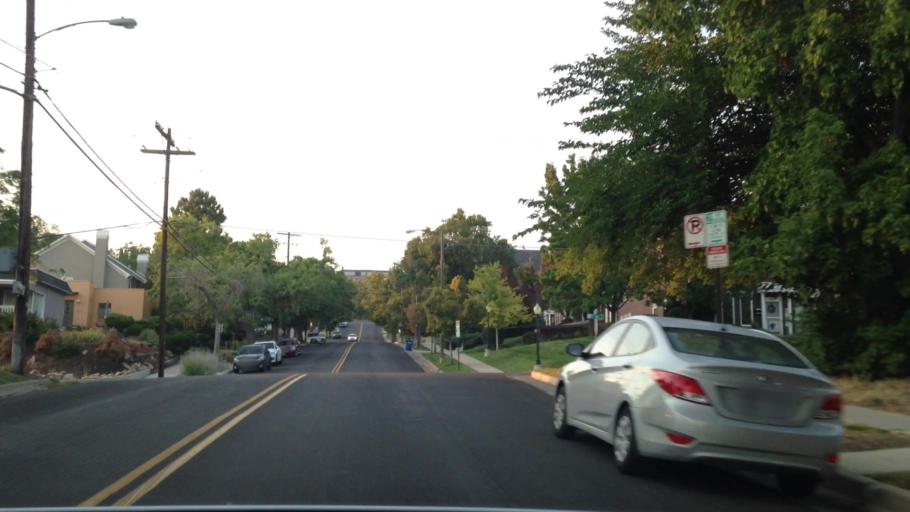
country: US
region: Utah
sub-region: Salt Lake County
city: Salt Lake City
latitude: 40.7786
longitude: -111.8776
